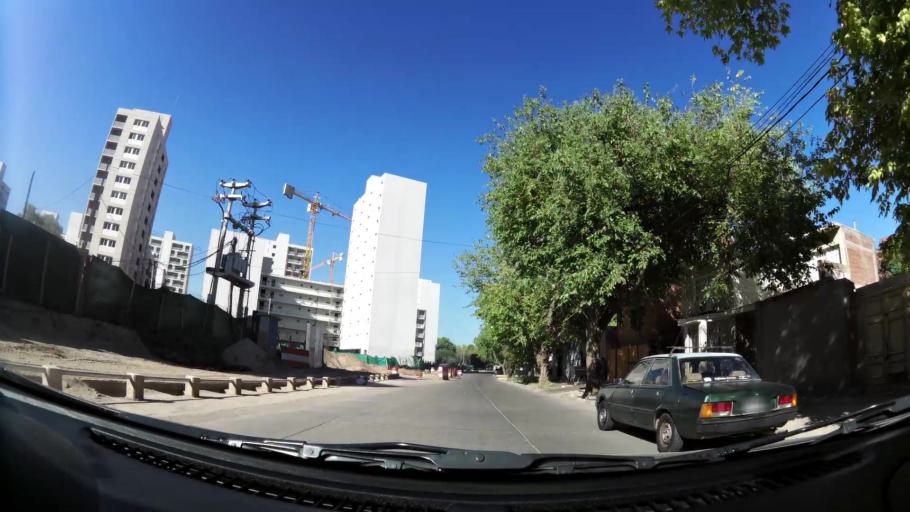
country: AR
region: Mendoza
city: Mendoza
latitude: -32.8761
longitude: -68.8481
